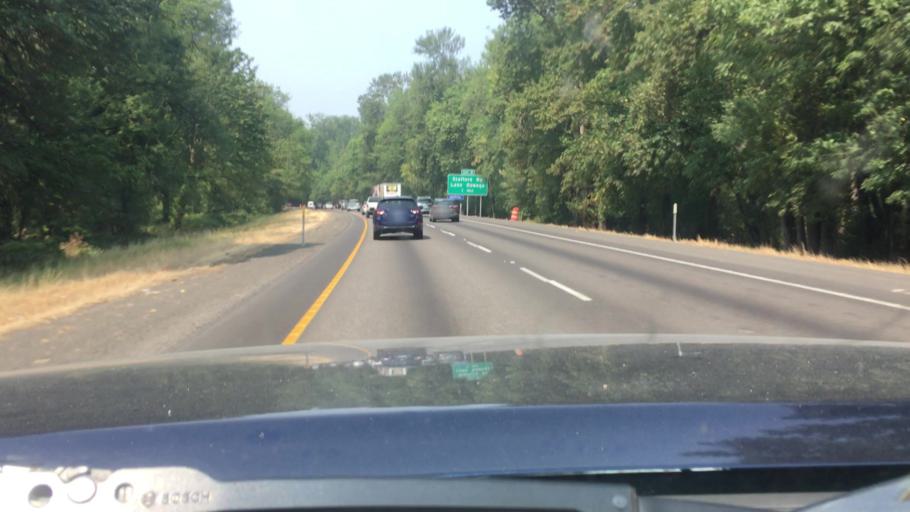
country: US
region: Oregon
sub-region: Clackamas County
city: Stafford
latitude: 45.3654
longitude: -122.6766
